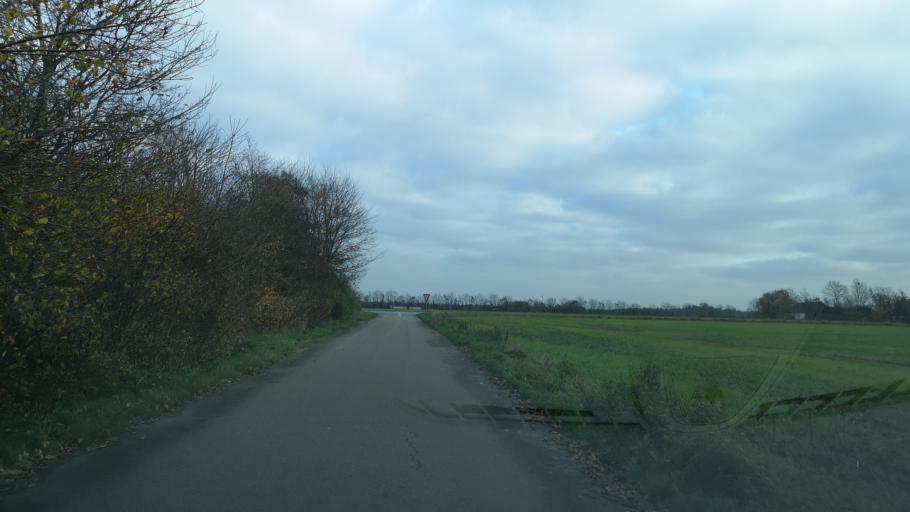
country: DK
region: Central Jutland
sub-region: Ringkobing-Skjern Kommune
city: Videbaek
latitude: 56.0317
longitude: 8.6064
